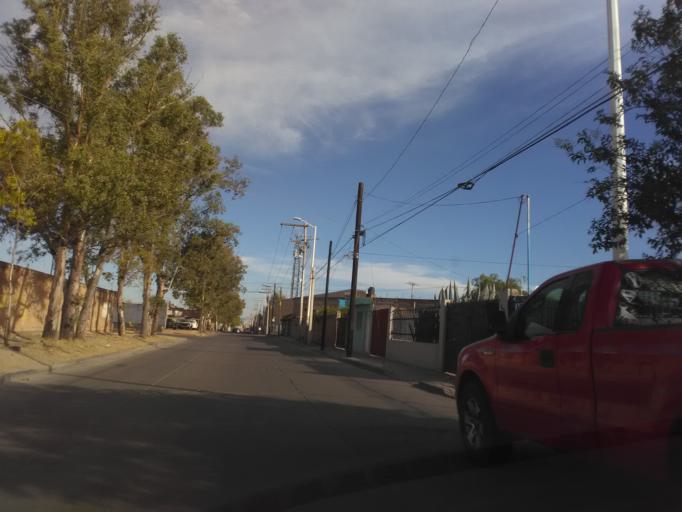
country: MX
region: Durango
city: Victoria de Durango
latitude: 24.0257
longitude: -104.6297
